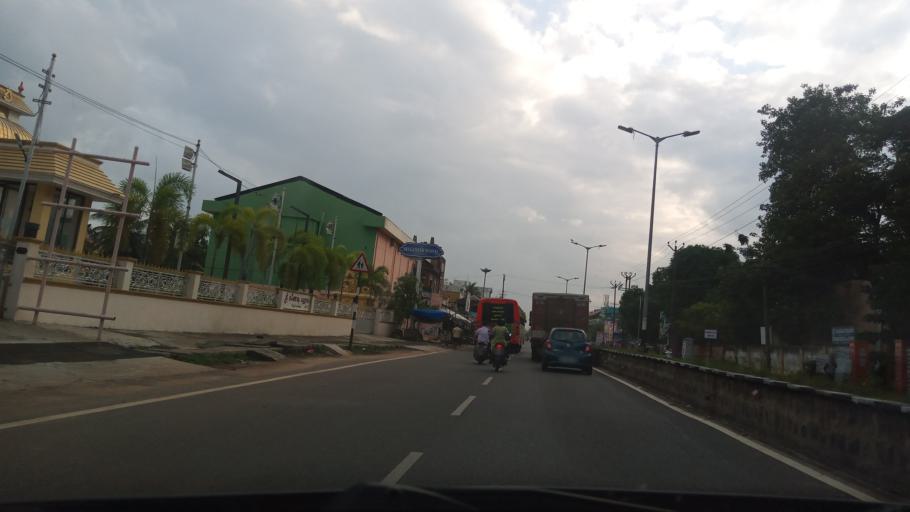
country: IN
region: Tamil Nadu
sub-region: Villupuram
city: Auroville
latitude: 12.0304
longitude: 79.8638
